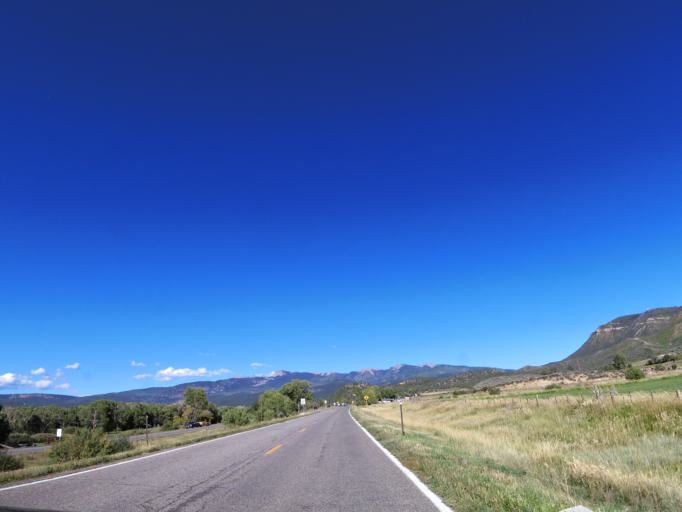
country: US
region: Colorado
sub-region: Montezuma County
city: Mancos
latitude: 37.3471
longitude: -108.2750
